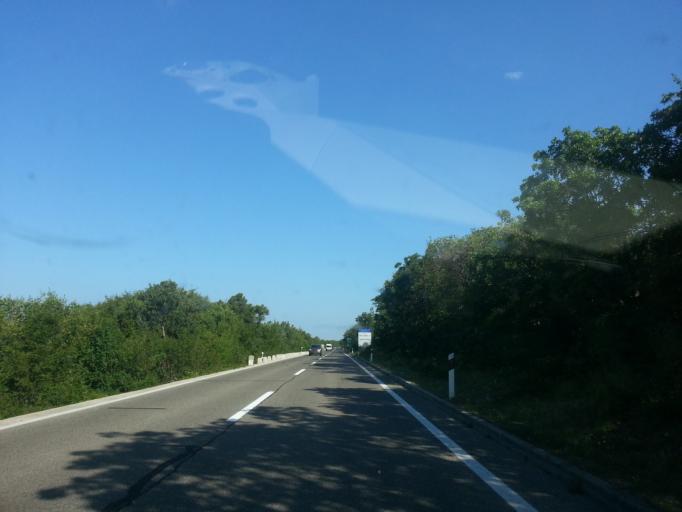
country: HR
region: Primorsko-Goranska
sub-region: Grad Crikvenica
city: Jadranovo
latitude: 45.2468
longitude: 14.6053
